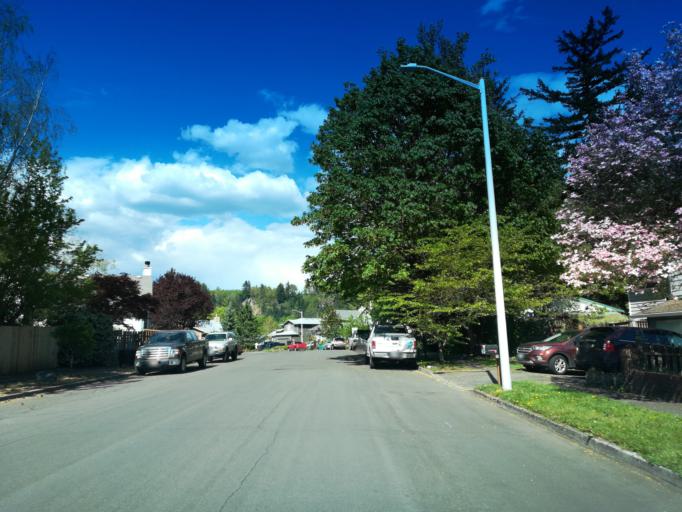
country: US
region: Oregon
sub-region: Multnomah County
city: Troutdale
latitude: 45.5332
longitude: -122.3817
